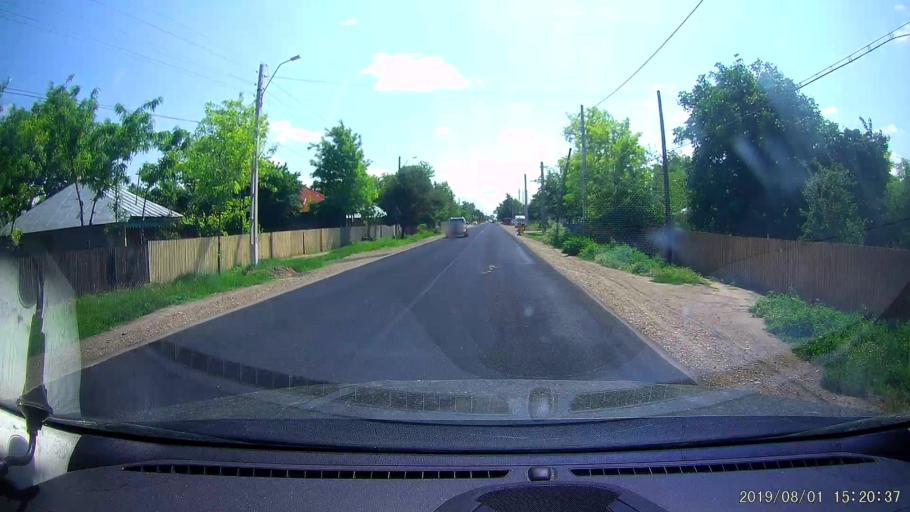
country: RO
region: Braila
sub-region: Comuna Tufesti
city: Tufesti
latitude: 45.0775
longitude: 27.8052
